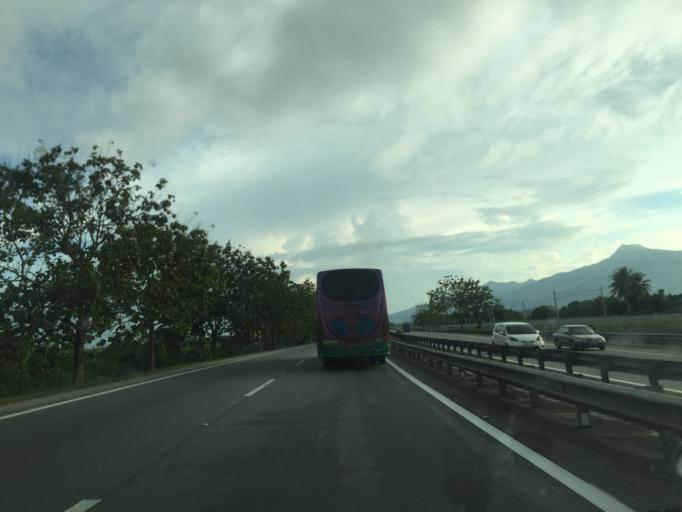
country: MY
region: Kedah
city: Gurun
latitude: 5.8914
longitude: 100.4774
